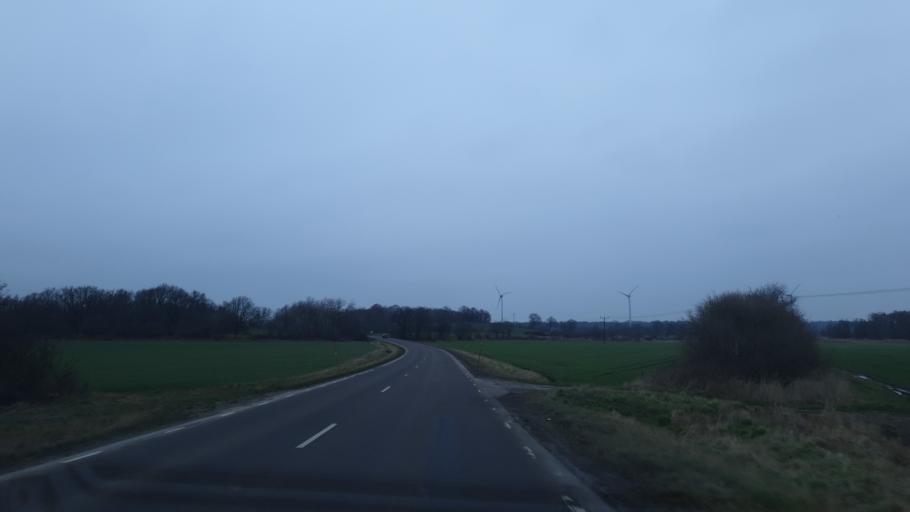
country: SE
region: Blekinge
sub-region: Karlskrona Kommun
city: Jaemjoe
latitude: 56.1548
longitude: 15.7633
